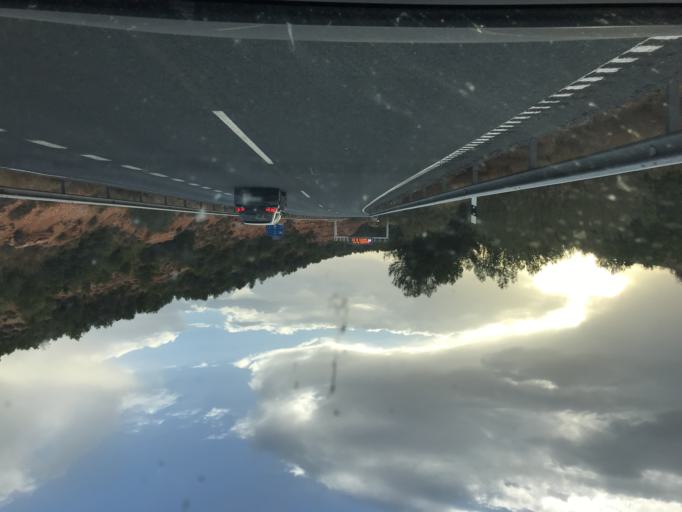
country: ES
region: Andalusia
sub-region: Provincia de Granada
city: Darro
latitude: 37.3245
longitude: -3.2531
